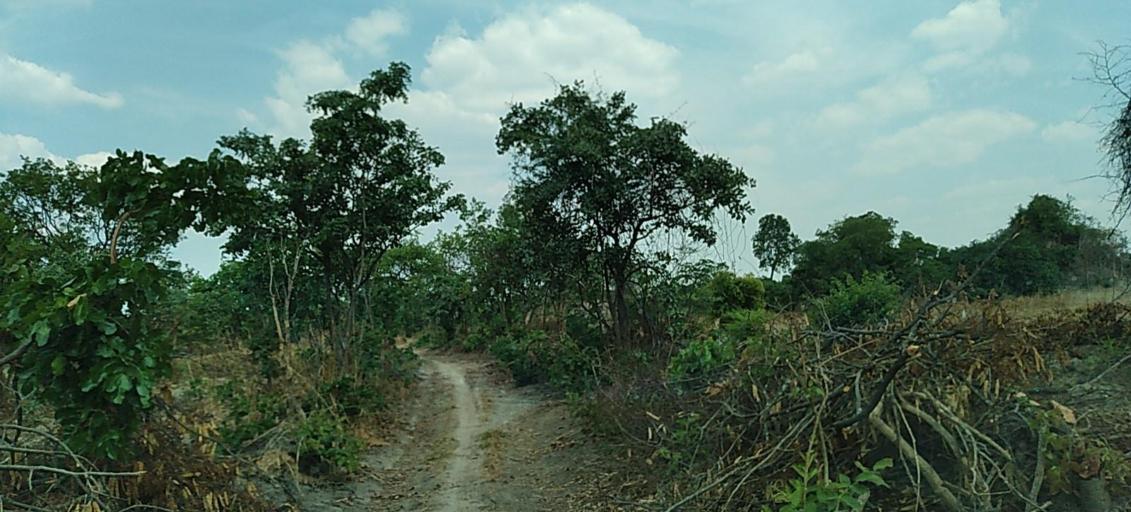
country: ZM
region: Copperbelt
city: Chililabombwe
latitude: -12.3404
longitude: 27.7803
